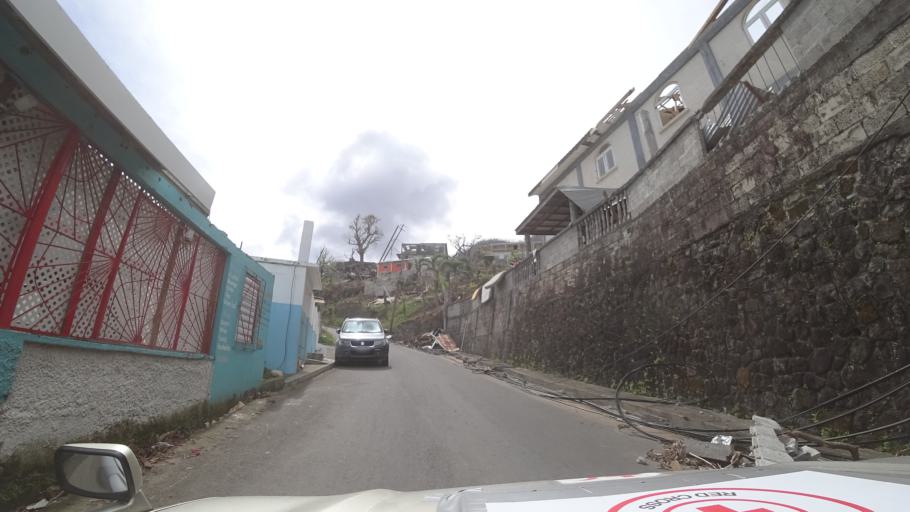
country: DM
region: Saint Patrick
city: Berekua
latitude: 15.2412
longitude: -61.3202
